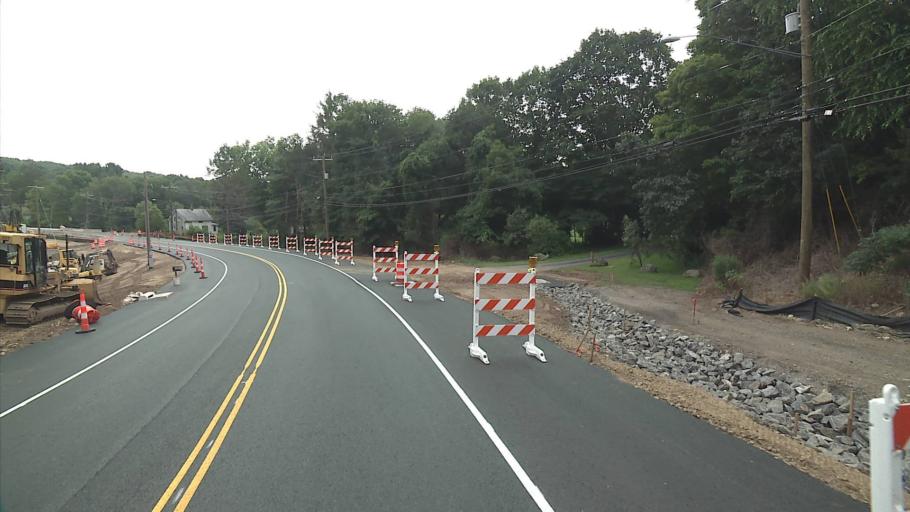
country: US
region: Connecticut
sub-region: Tolland County
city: Tolland
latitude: 41.8825
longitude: -72.3084
